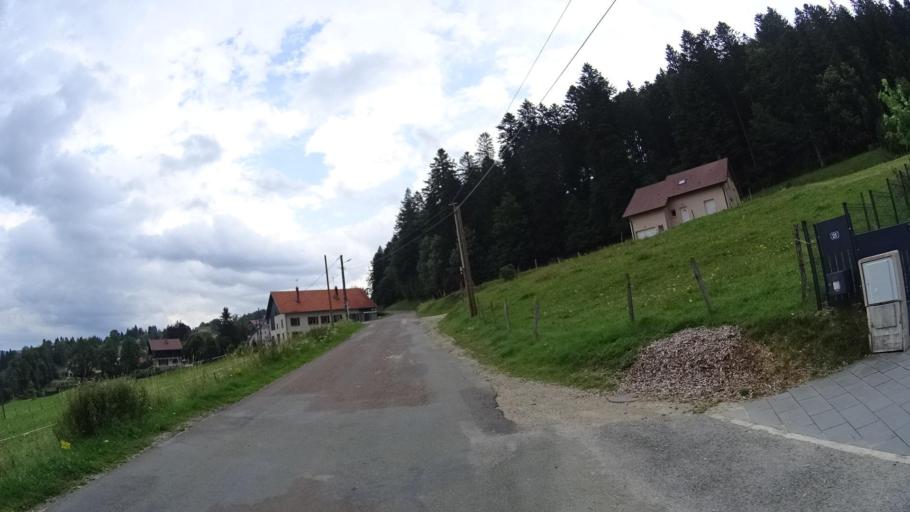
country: FR
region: Franche-Comte
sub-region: Departement du Doubs
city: Les Fourgs
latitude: 46.8240
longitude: 6.3367
